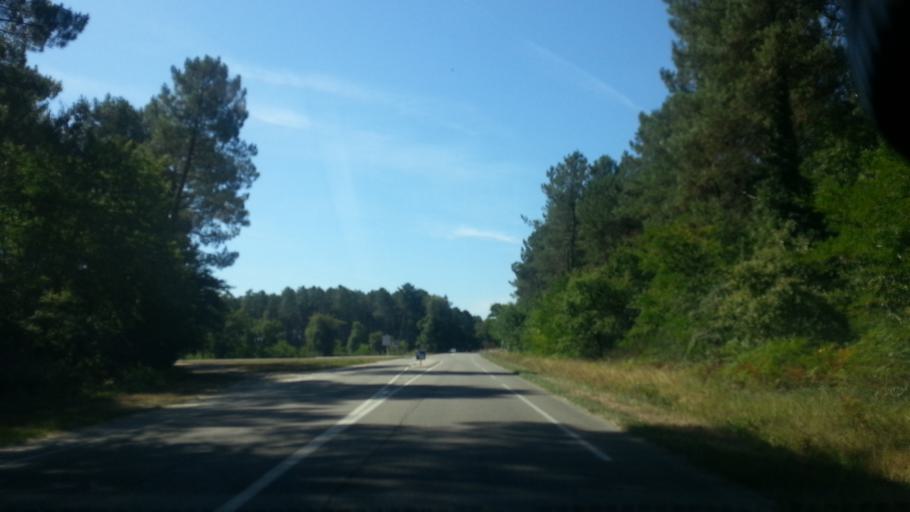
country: FR
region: Aquitaine
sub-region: Departement de la Gironde
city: Illats
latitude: 44.6135
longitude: -0.3724
